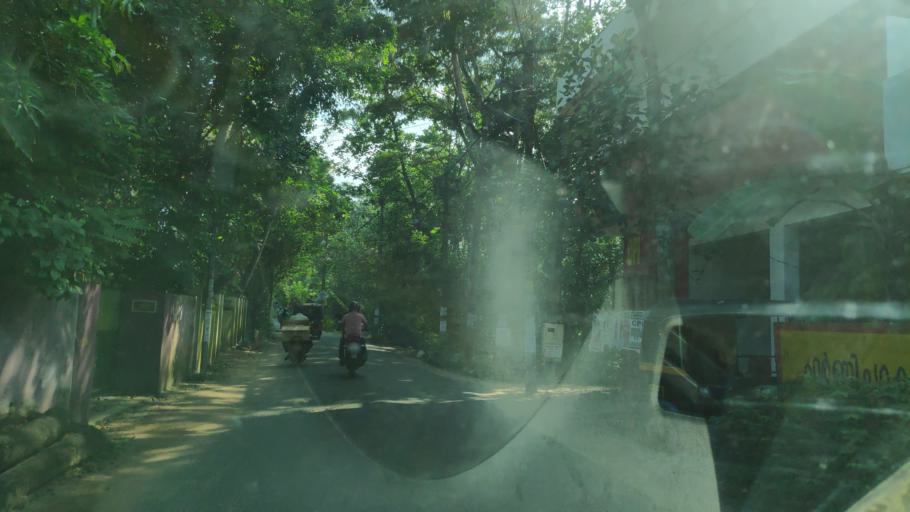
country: IN
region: Kerala
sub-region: Alappuzha
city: Alleppey
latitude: 9.5097
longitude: 76.3201
